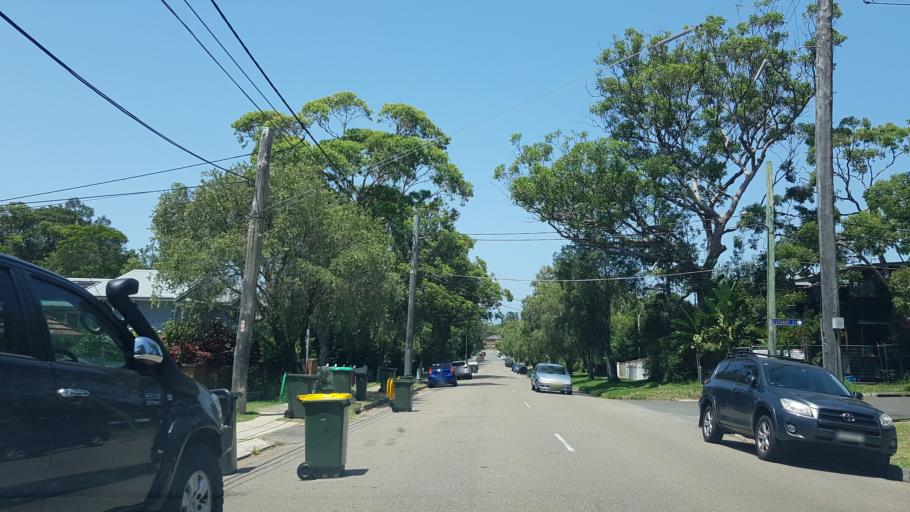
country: AU
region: New South Wales
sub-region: Pittwater
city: Newport
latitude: -33.6583
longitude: 151.3124
